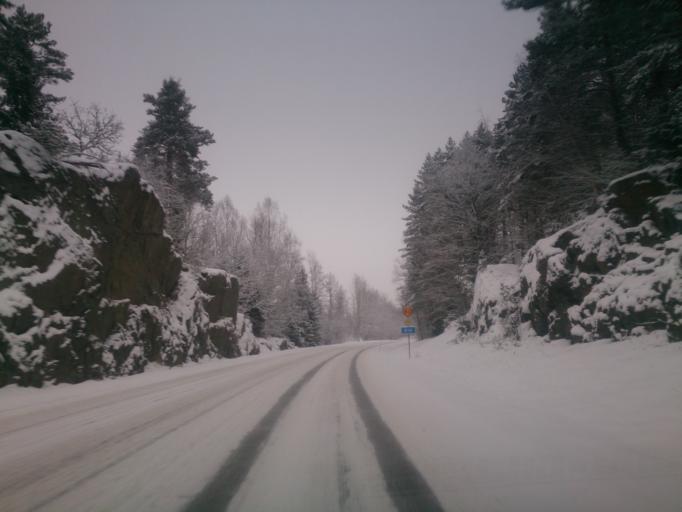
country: SE
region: OEstergoetland
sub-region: Finspangs Kommun
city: Finspang
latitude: 58.6188
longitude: 15.8126
